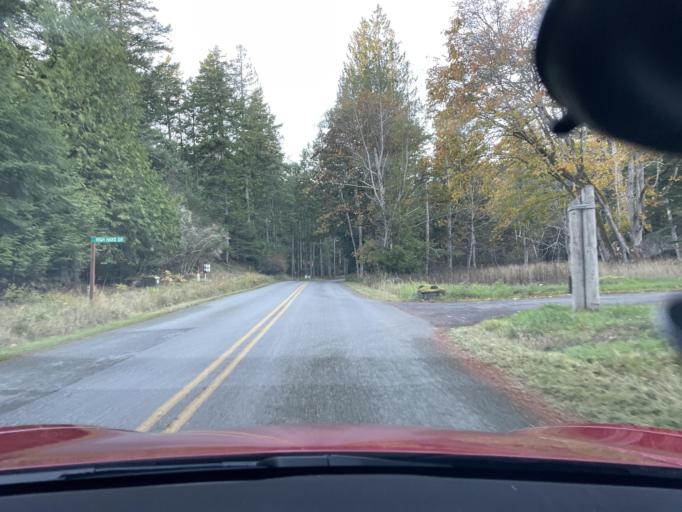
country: US
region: Washington
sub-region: San Juan County
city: Friday Harbor
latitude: 48.5298
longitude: -123.1546
